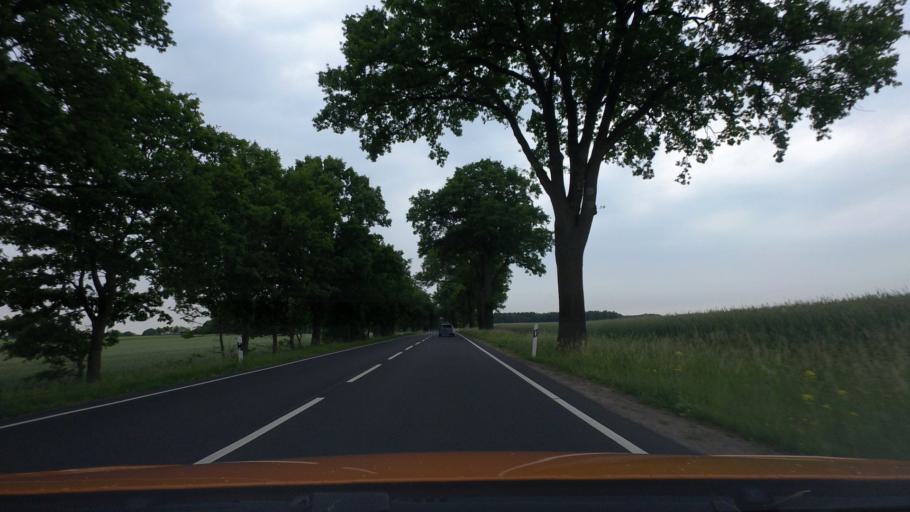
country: DE
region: Lower Saxony
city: Wietzen
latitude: 52.6844
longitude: 9.0999
